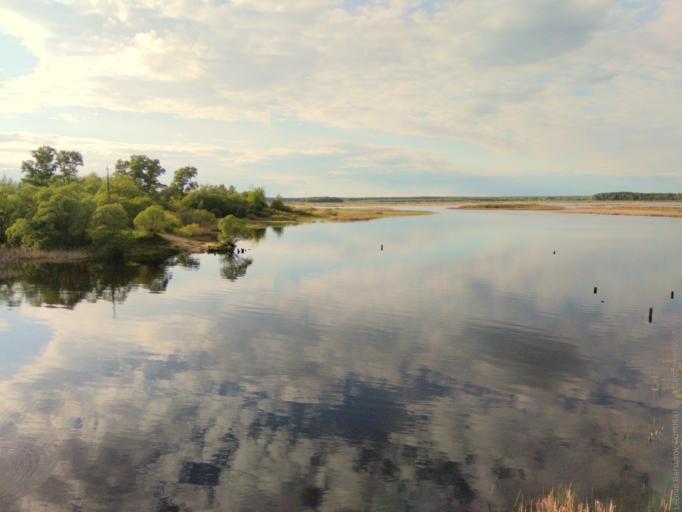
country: RU
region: Rjazan
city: Spas-Klepiki
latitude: 55.2186
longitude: 40.1004
